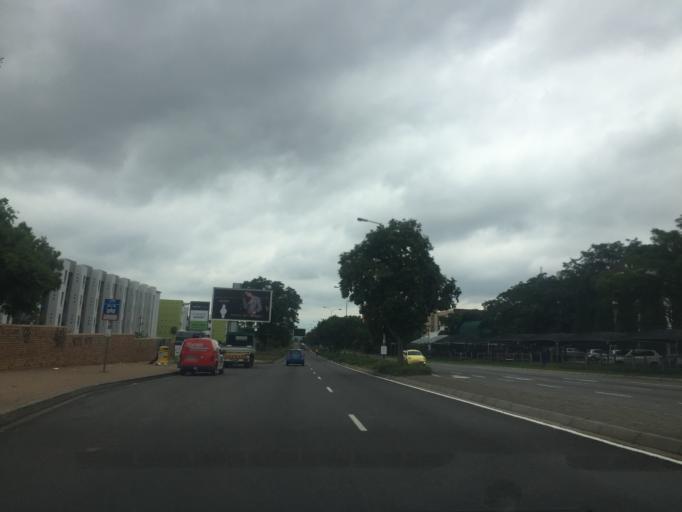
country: ZA
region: Gauteng
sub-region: City of Johannesburg Metropolitan Municipality
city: Midrand
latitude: -26.0543
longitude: 28.0589
